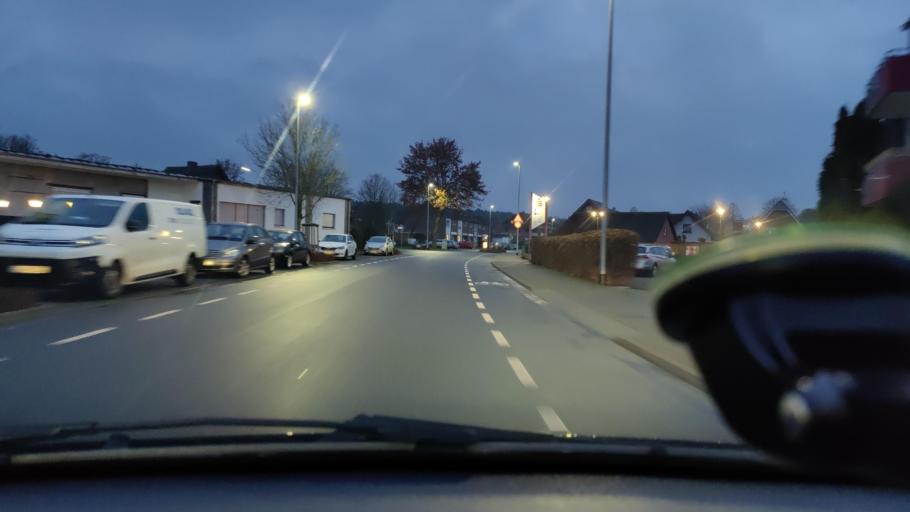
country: DE
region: North Rhine-Westphalia
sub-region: Regierungsbezirk Dusseldorf
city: Xanten
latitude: 51.6521
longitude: 6.4443
